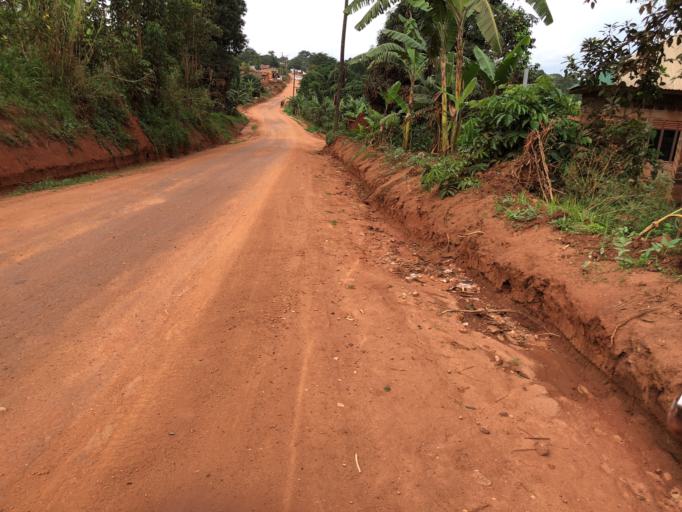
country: UG
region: Central Region
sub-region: Wakiso District
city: Bweyogerere
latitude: 0.4803
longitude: 32.6421
